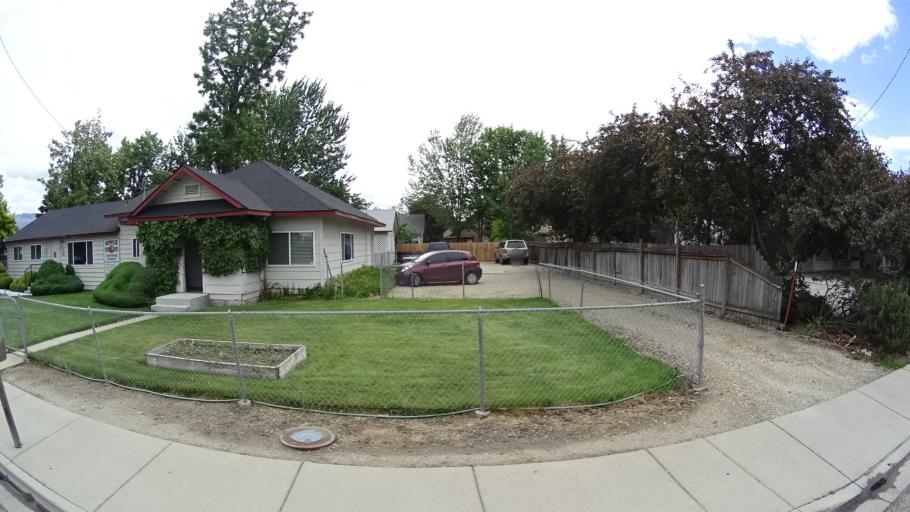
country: US
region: Idaho
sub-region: Ada County
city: Boise
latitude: 43.5757
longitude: -116.1733
